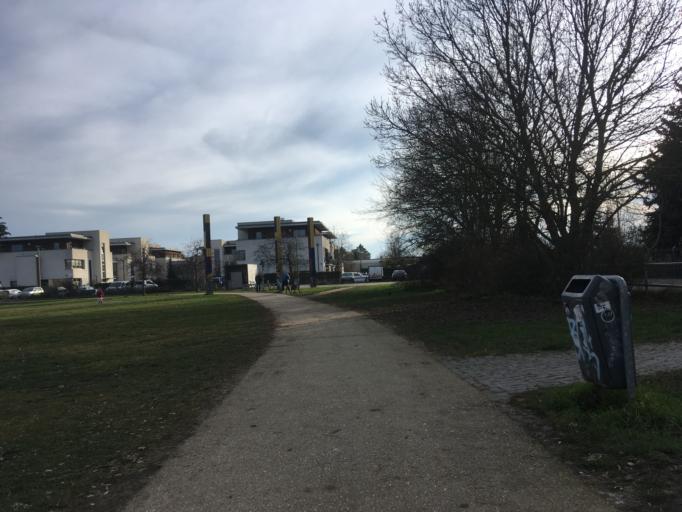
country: DE
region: Berlin
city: Biesdorf
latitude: 52.5015
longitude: 13.5467
